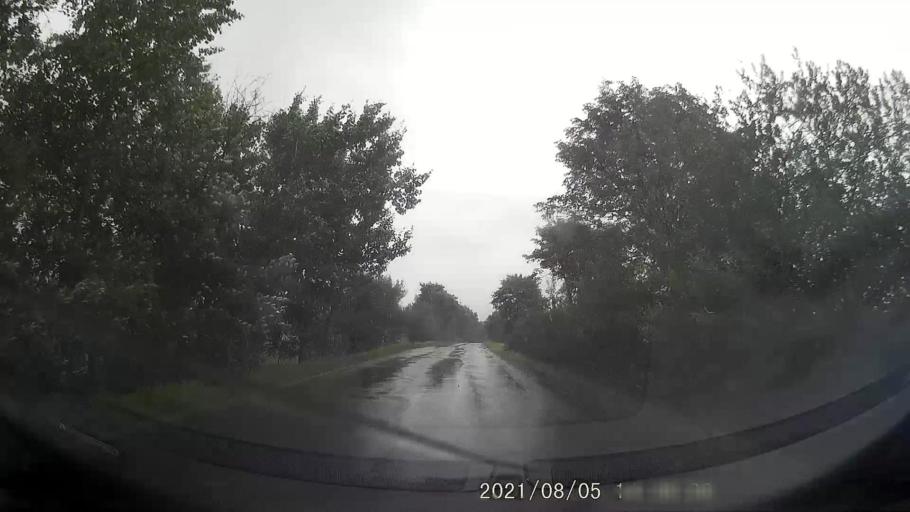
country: PL
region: Opole Voivodeship
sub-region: Powiat nyski
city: Lambinowice
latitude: 50.4660
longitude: 17.4893
